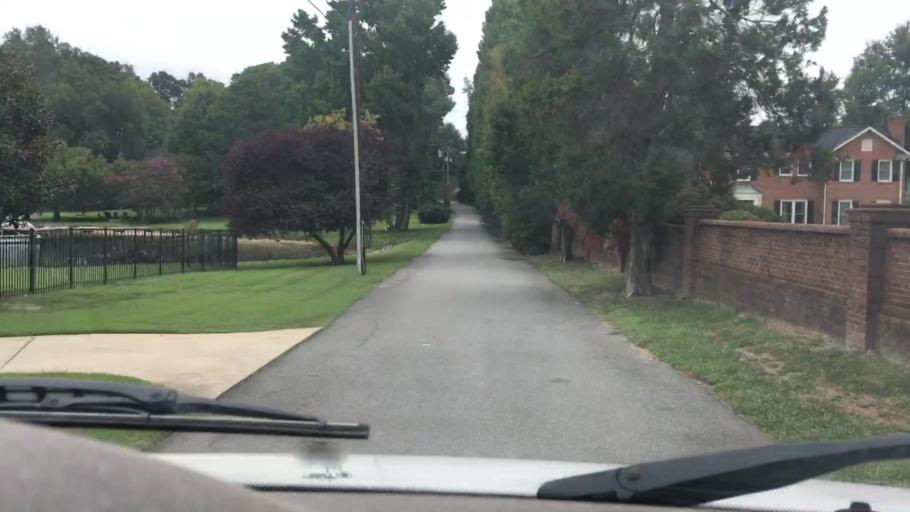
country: US
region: North Carolina
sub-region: Mecklenburg County
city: Cornelius
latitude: 35.4481
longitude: -80.9003
